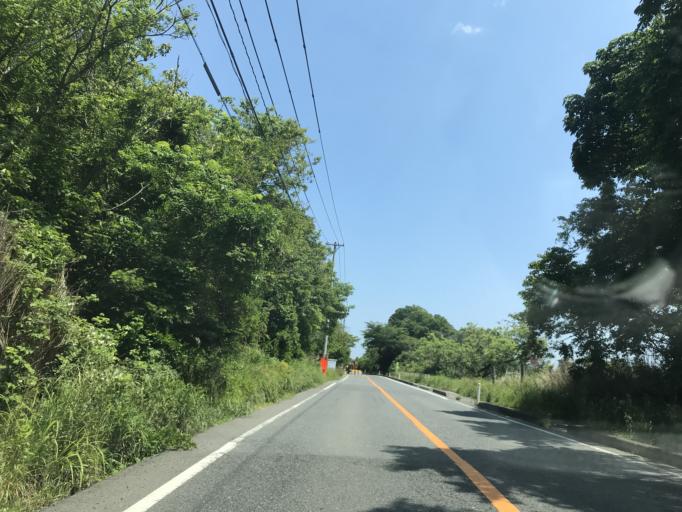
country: JP
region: Miyagi
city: Matsushima
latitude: 38.3809
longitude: 141.1225
